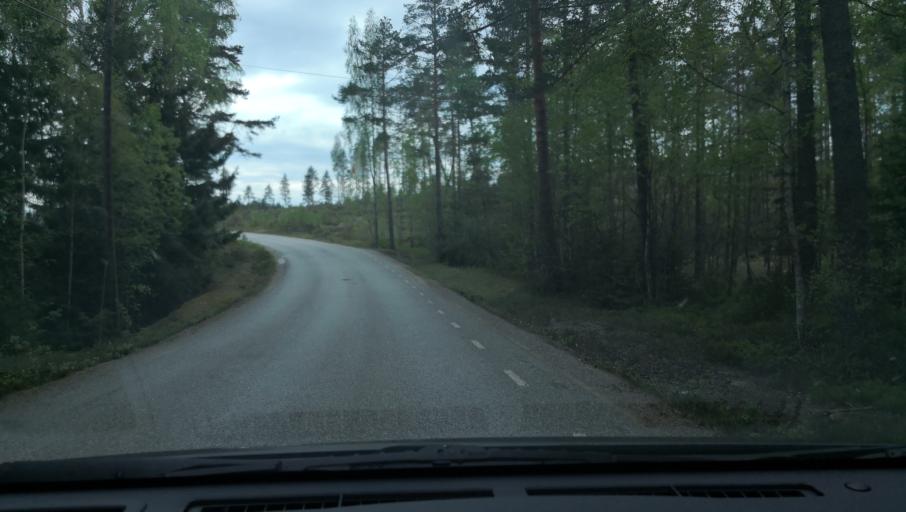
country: SE
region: Vaestmanland
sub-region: Skinnskattebergs Kommun
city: Skinnskatteberg
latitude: 59.8239
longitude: 15.5512
